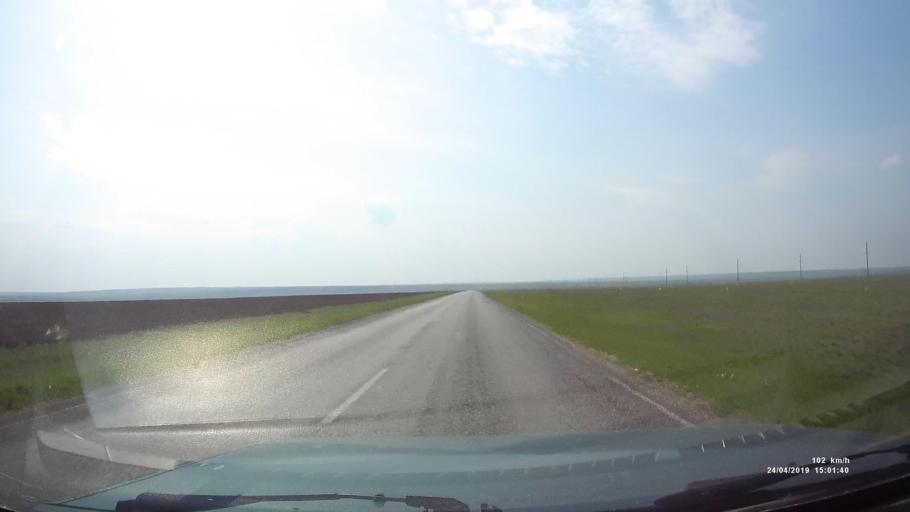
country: RU
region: Rostov
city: Remontnoye
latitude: 46.5663
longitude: 43.5287
